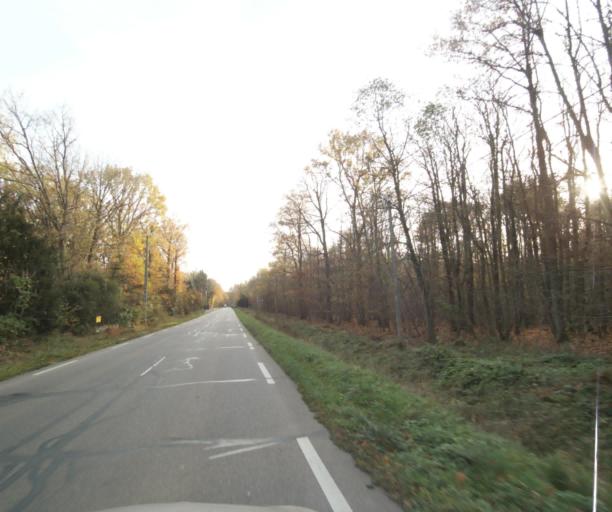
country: FR
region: Ile-de-France
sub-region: Departement des Yvelines
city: Chanteloup-les-Vignes
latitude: 48.9886
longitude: 2.0246
